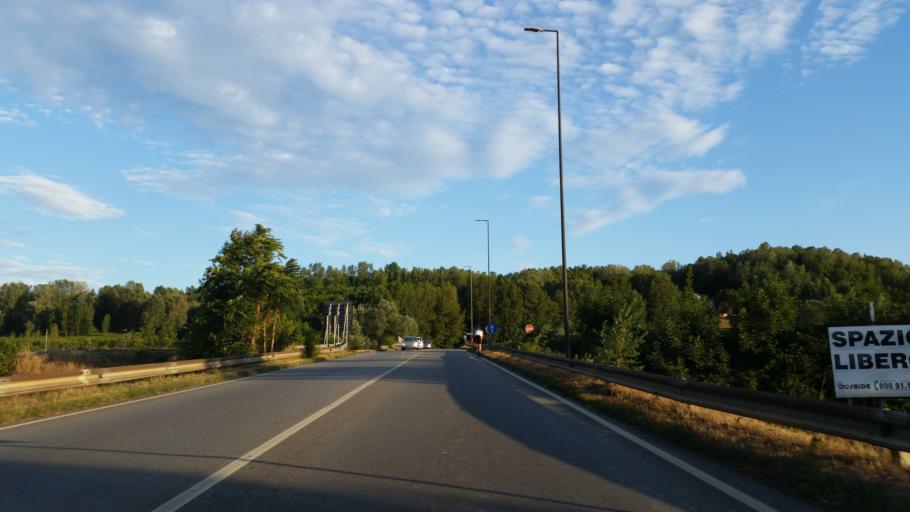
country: IT
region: Piedmont
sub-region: Provincia di Asti
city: Asti
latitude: 44.8767
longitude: 8.2150
